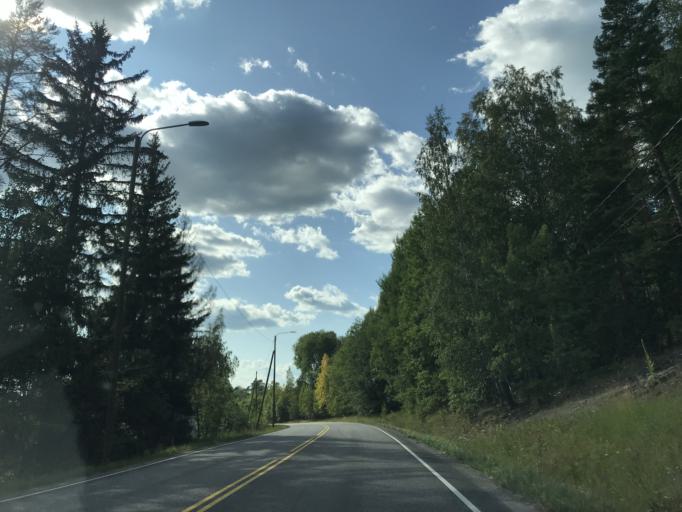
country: FI
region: Uusimaa
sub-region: Helsinki
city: Nurmijaervi
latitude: 60.4635
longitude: 24.7566
